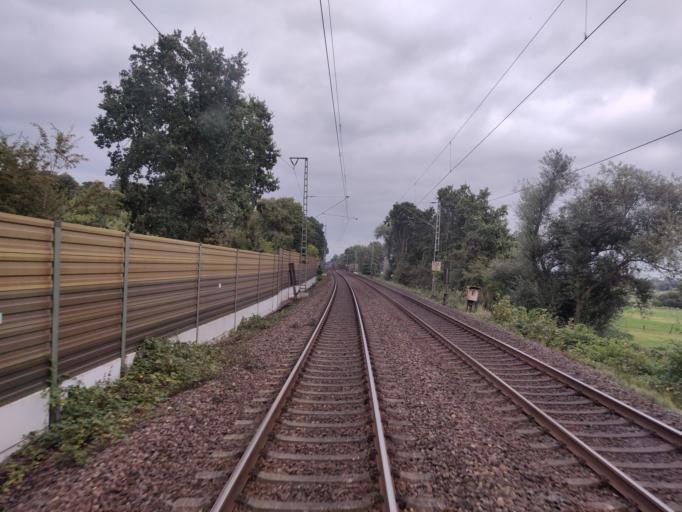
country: DE
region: Lower Saxony
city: Ritterhude
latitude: 53.1710
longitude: 8.7281
